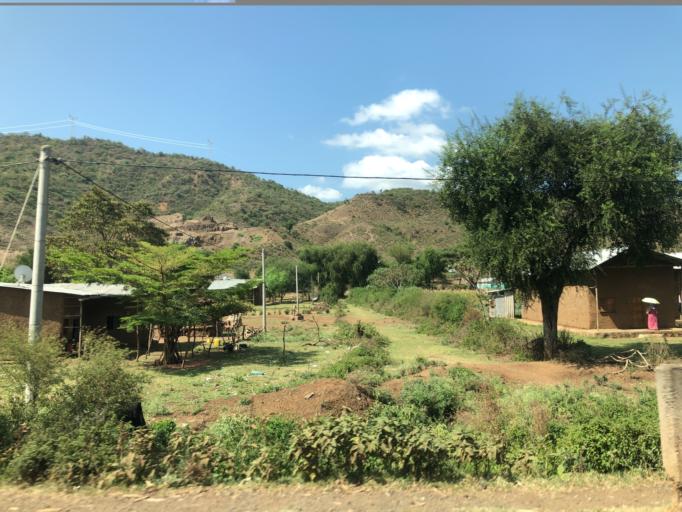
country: ET
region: Southern Nations, Nationalities, and People's Region
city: Gidole
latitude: 5.8195
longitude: 37.4561
